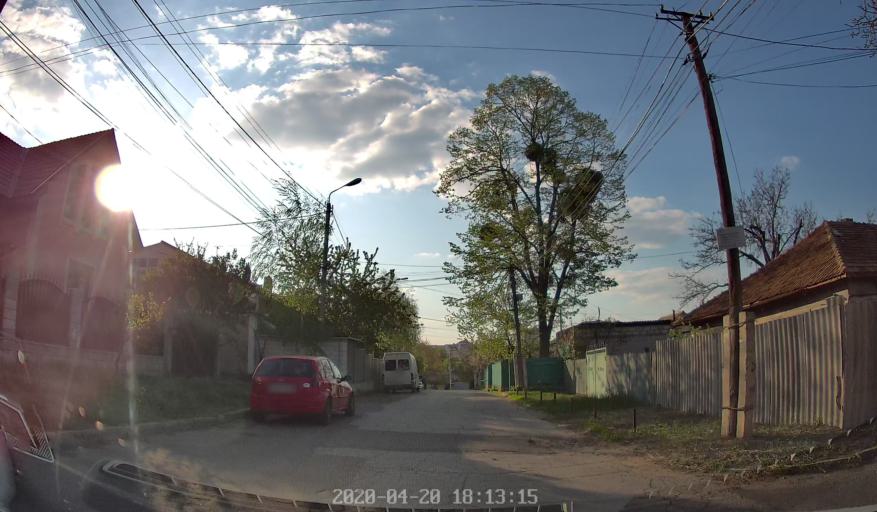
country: MD
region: Chisinau
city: Chisinau
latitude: 46.9976
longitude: 28.8293
